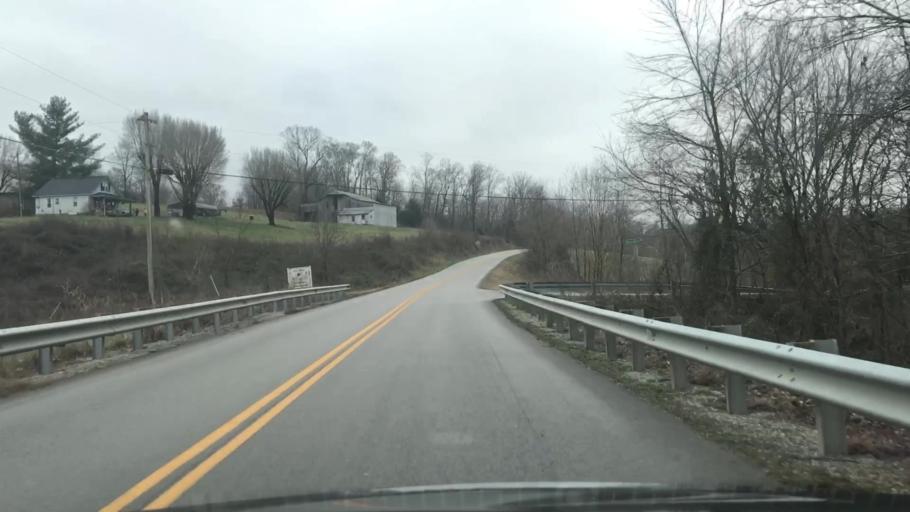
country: US
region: Kentucky
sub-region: Monroe County
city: Tompkinsville
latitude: 36.8514
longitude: -85.7705
